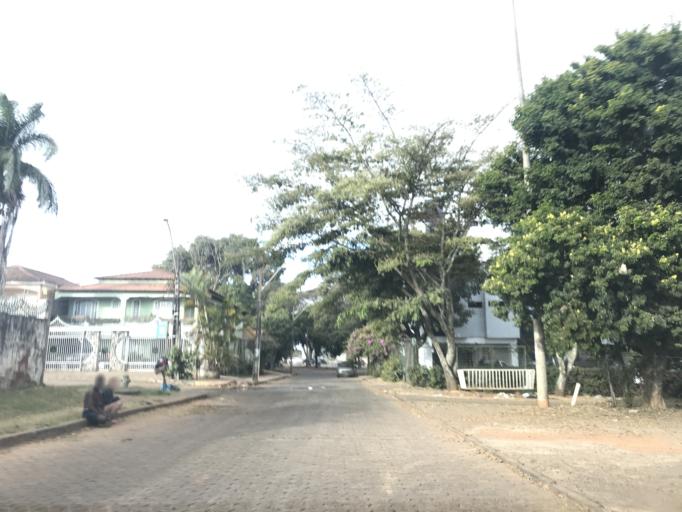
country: BR
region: Federal District
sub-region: Brasilia
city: Brasilia
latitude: -15.8027
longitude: -48.0585
